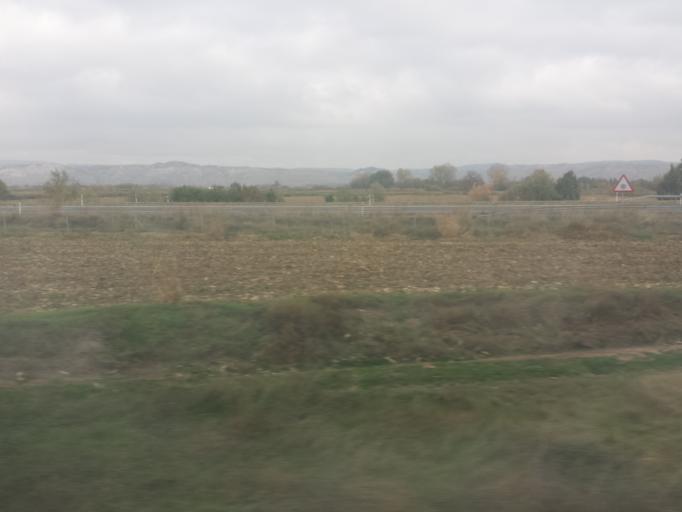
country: ES
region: Aragon
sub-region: Provincia de Zaragoza
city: Alagon
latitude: 41.7651
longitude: -1.0997
